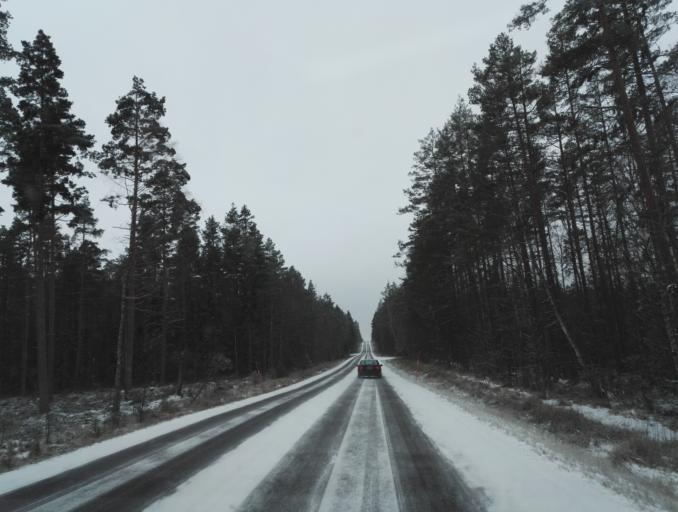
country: SE
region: Kronoberg
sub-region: Lessebo Kommun
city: Lessebo
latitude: 56.7660
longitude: 15.2925
